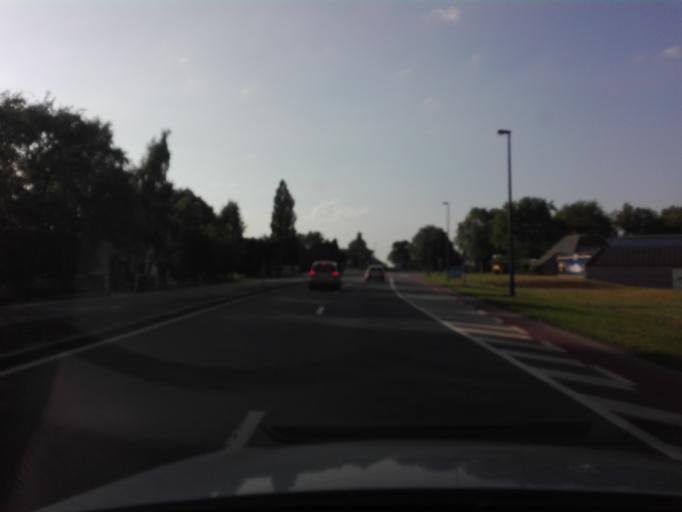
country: BE
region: Wallonia
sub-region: Province du Brabant Wallon
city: Louvain-la-Neuve
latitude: 50.6615
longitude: 4.6330
